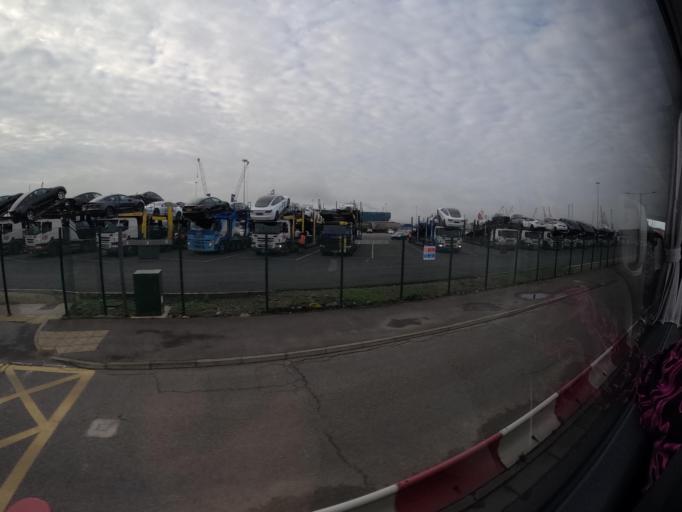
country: GB
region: England
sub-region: Southampton
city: Southampton
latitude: 50.9053
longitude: -1.4235
